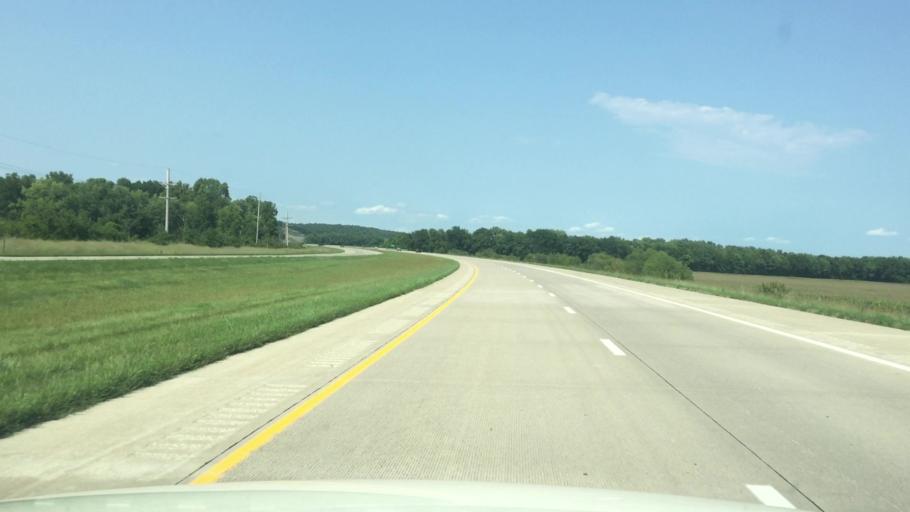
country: US
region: Kansas
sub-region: Linn County
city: Pleasanton
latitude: 38.2310
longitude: -94.6933
